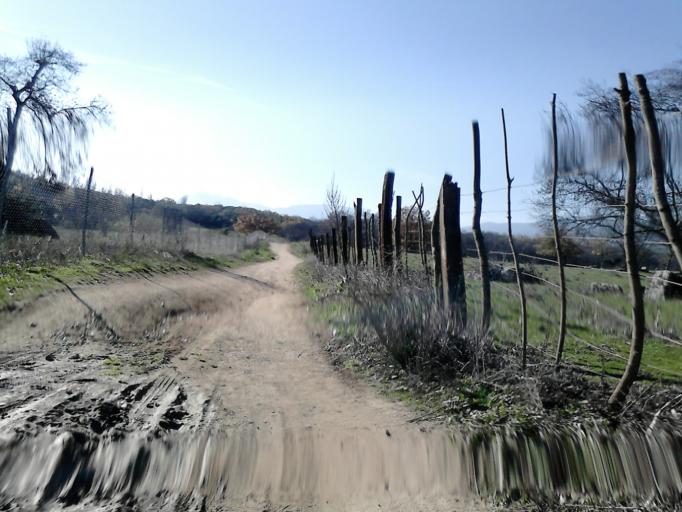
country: ES
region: Madrid
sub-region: Provincia de Madrid
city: Navalquejigo
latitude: 40.6110
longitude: -4.0868
